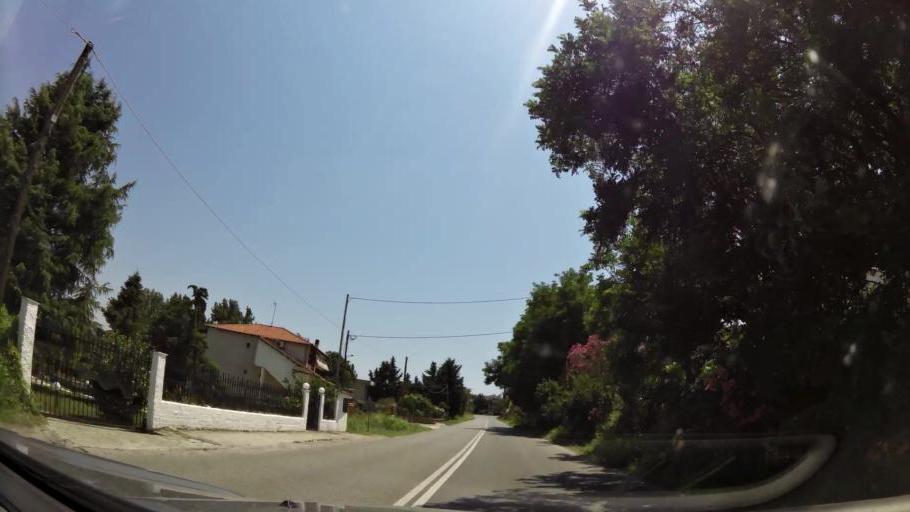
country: GR
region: Central Macedonia
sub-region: Nomos Thessalonikis
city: Trilofos
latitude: 40.4740
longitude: 22.9728
